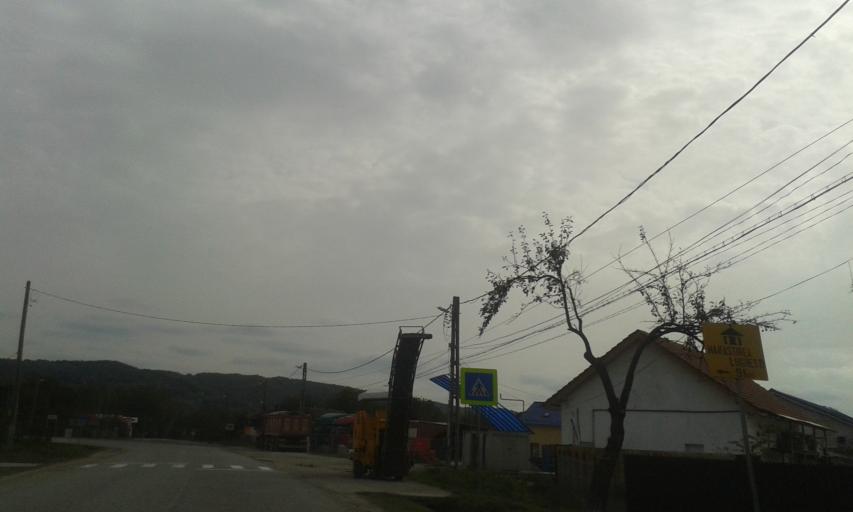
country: RO
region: Gorj
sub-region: Comuna Hurezani
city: Hurezani
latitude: 44.8172
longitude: 23.6527
